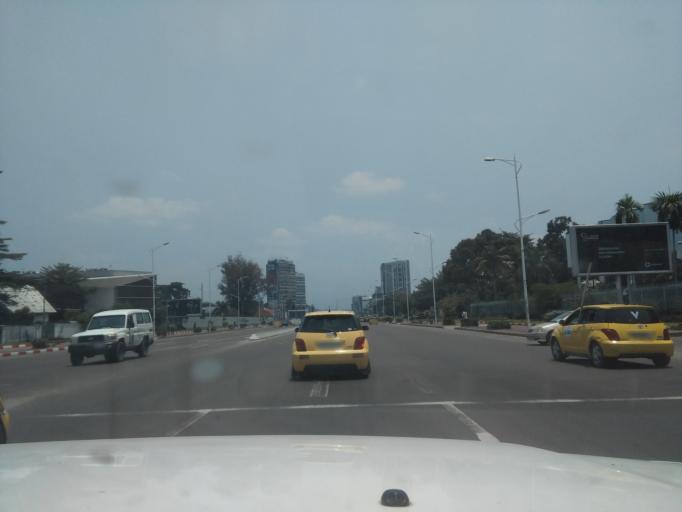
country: CD
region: Kinshasa
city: Kinshasa
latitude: -4.3093
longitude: 15.2909
